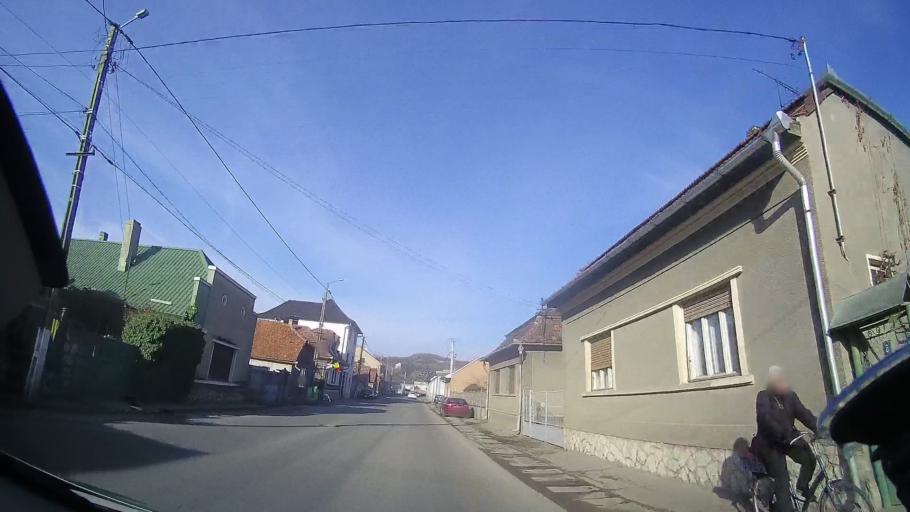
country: RO
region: Bihor
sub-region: Oras Alesd
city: Pestis
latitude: 47.0582
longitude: 22.3909
